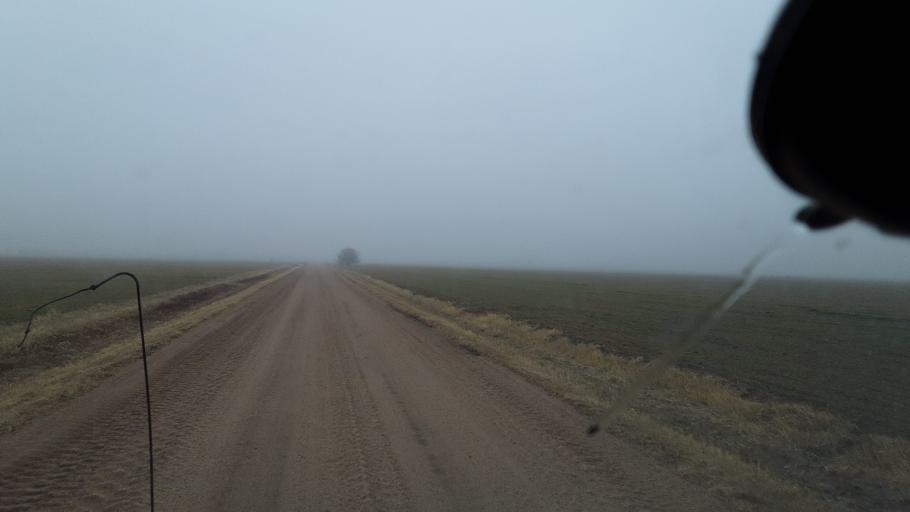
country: US
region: Kansas
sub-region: Reno County
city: South Hutchinson
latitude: 37.9747
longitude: -97.9954
